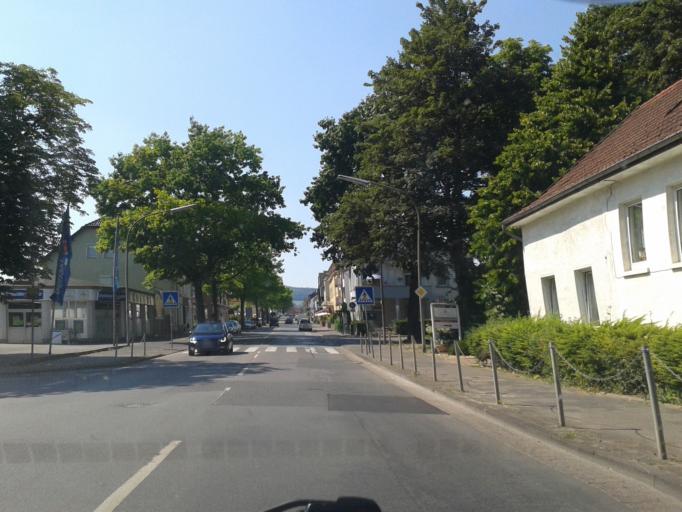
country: DE
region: Lower Saxony
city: Bad Pyrmont
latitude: 51.9826
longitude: 9.2463
